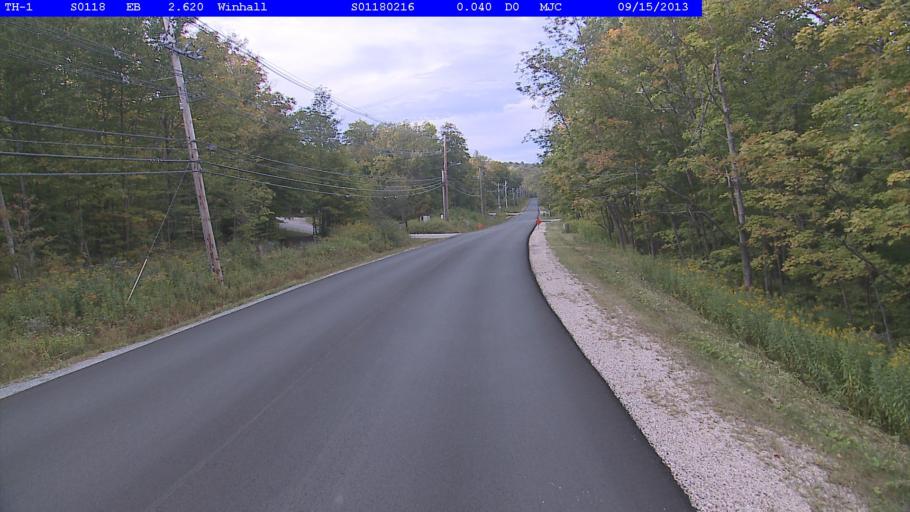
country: US
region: Vermont
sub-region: Bennington County
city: Manchester Center
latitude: 43.1160
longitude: -72.9096
